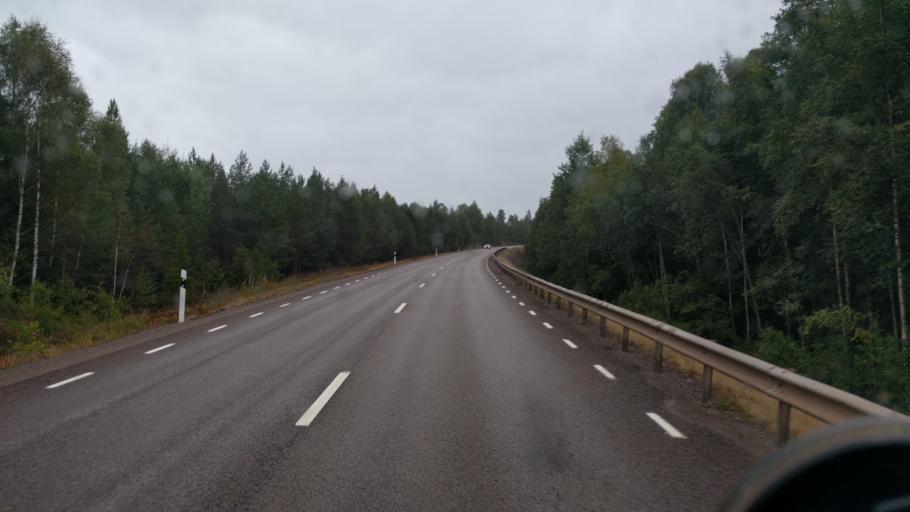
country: SE
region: Kalmar
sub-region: Vasterviks Kommun
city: Ankarsrum
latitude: 57.7034
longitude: 16.1899
